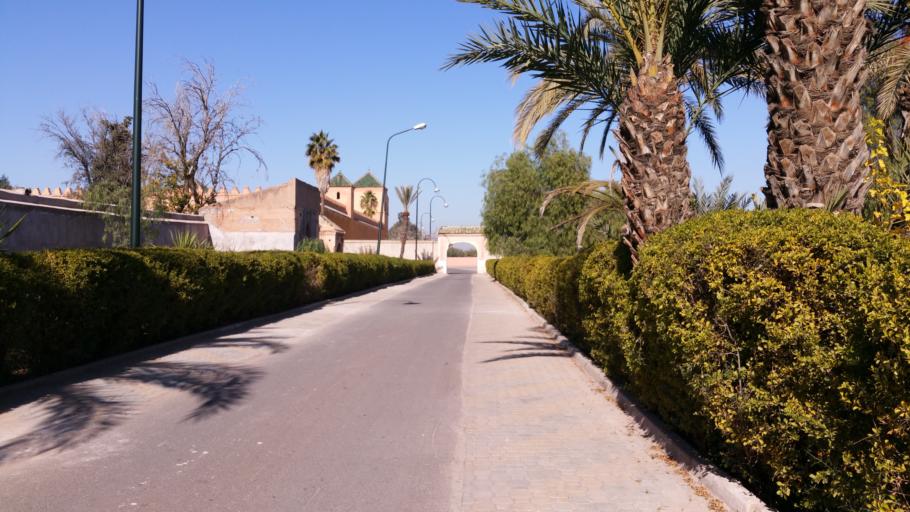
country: MA
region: Marrakech-Tensift-Al Haouz
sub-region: Marrakech
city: Marrakesh
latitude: 31.6023
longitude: -7.9800
